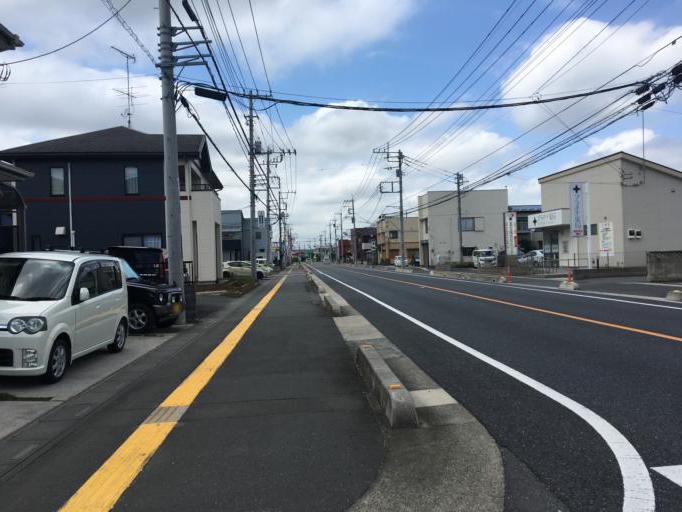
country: JP
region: Saitama
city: Okegawa
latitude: 35.9913
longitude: 139.5749
